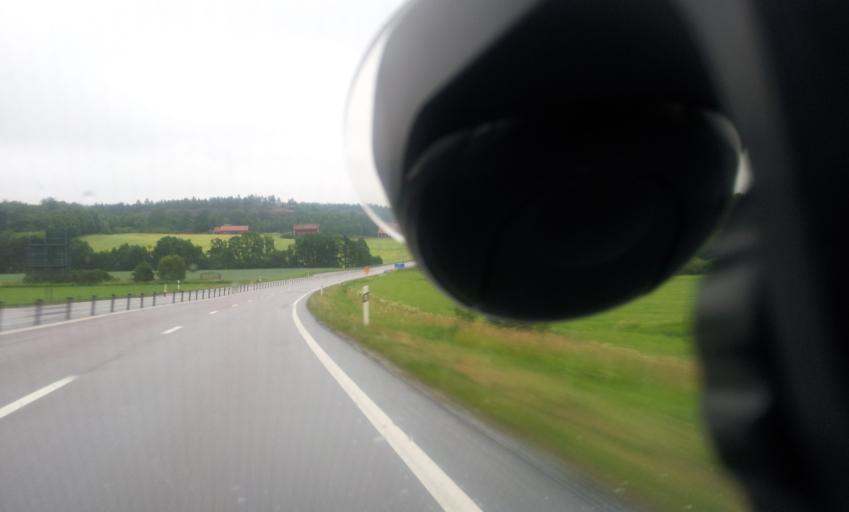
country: SE
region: Kalmar
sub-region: Vasterviks Kommun
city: Forserum
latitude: 58.0061
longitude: 16.4910
